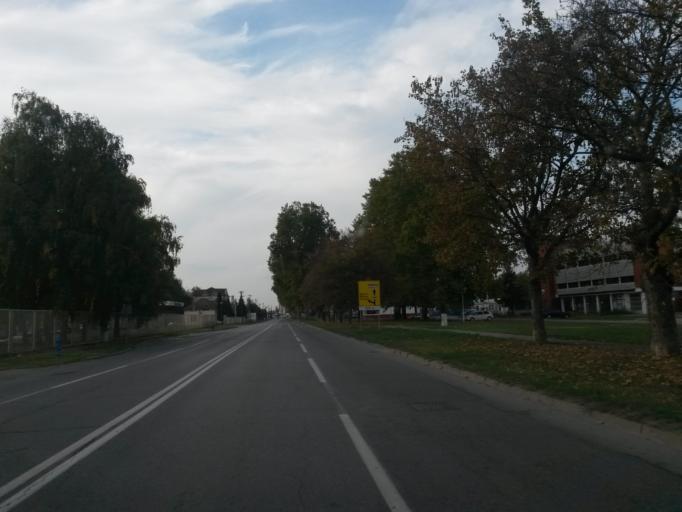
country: HR
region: Osjecko-Baranjska
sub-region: Grad Osijek
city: Osijek
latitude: 45.5482
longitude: 18.7382
